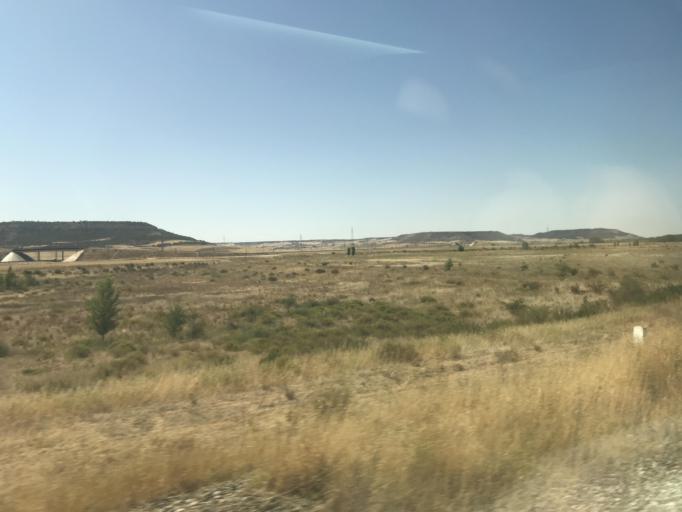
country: ES
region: Castille and Leon
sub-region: Provincia de Palencia
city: Torquemada
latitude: 42.0086
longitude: -4.3177
